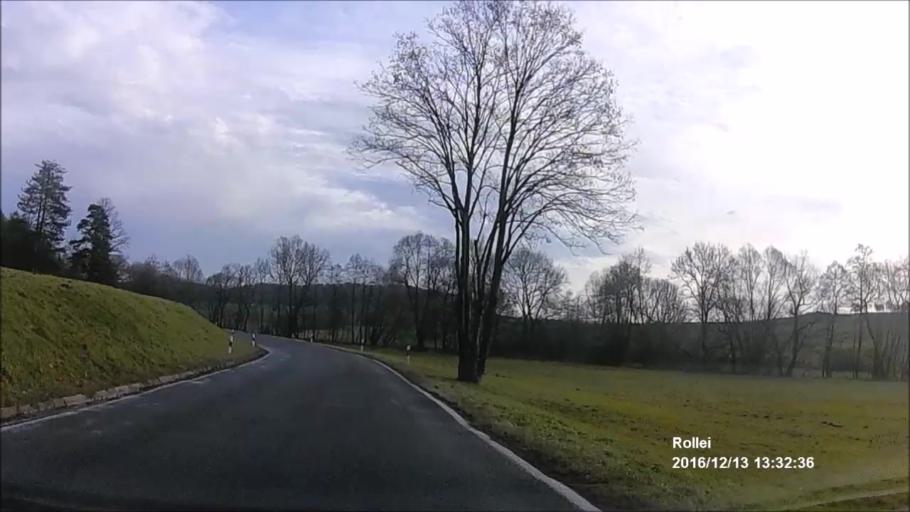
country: DE
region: Thuringia
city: Rittersdorf
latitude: 50.8523
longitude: 11.2666
